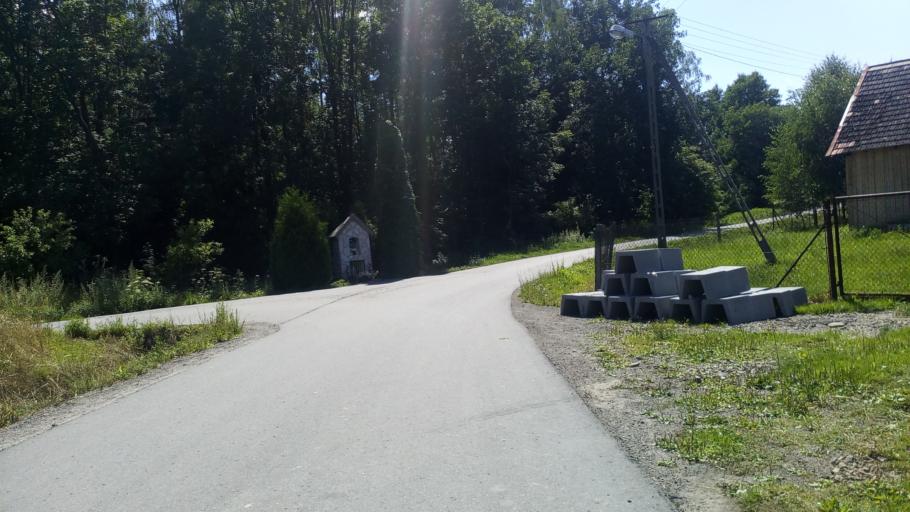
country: PL
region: Lesser Poland Voivodeship
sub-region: Powiat nowosadecki
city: Olszana
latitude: 49.5625
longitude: 20.5111
